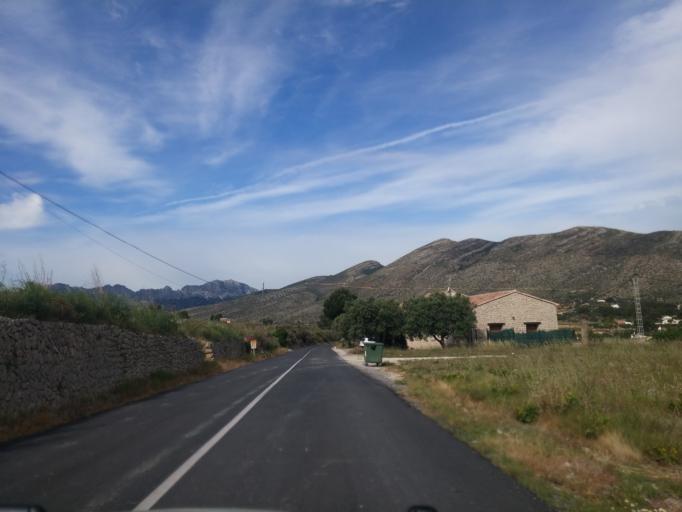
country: ES
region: Valencia
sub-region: Provincia de Alicante
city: Benissa
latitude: 38.7101
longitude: 0.0345
